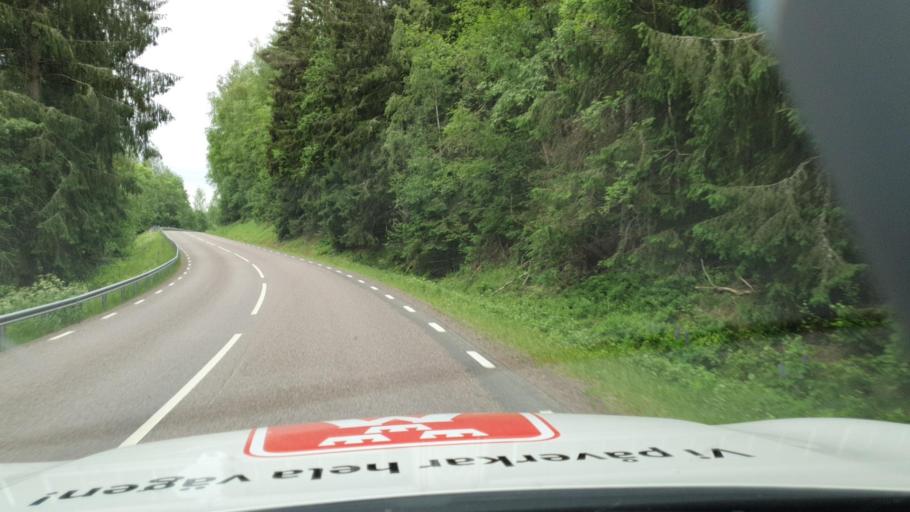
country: SE
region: Vaermland
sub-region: Sunne Kommun
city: Sunne
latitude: 59.8250
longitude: 12.9912
